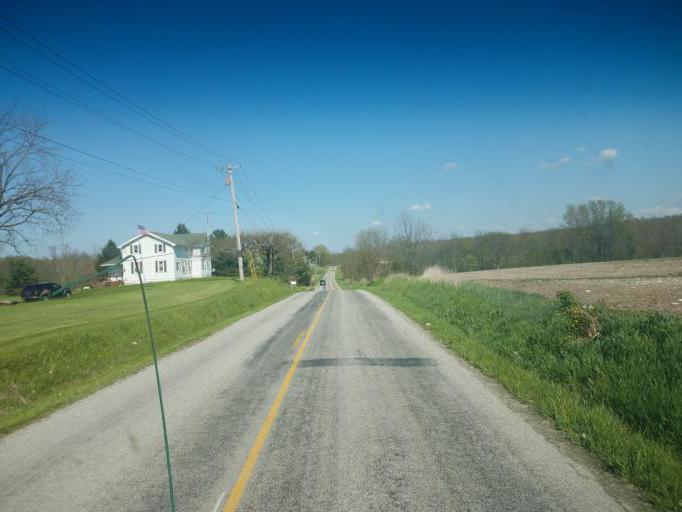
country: US
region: Ohio
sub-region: Medina County
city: Lodi
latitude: 40.9871
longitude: -82.0283
